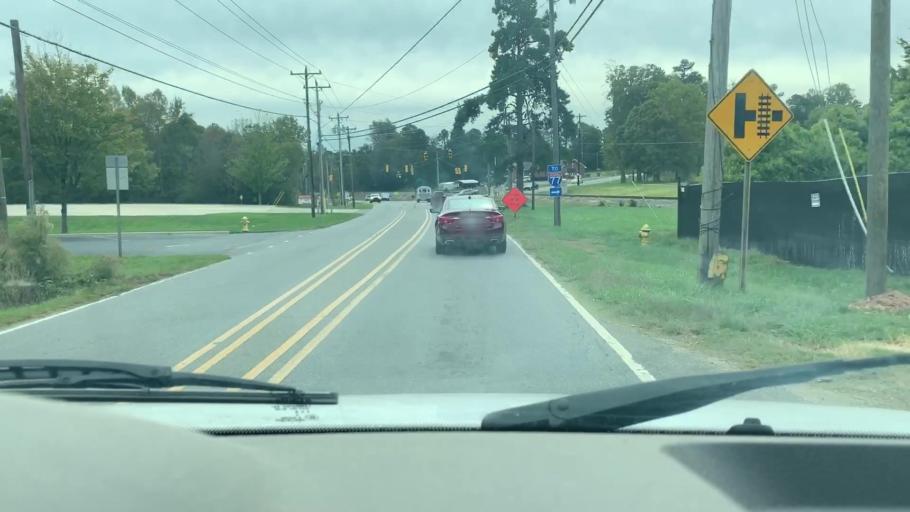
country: US
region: North Carolina
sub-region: Gaston County
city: Davidson
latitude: 35.5403
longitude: -80.8478
